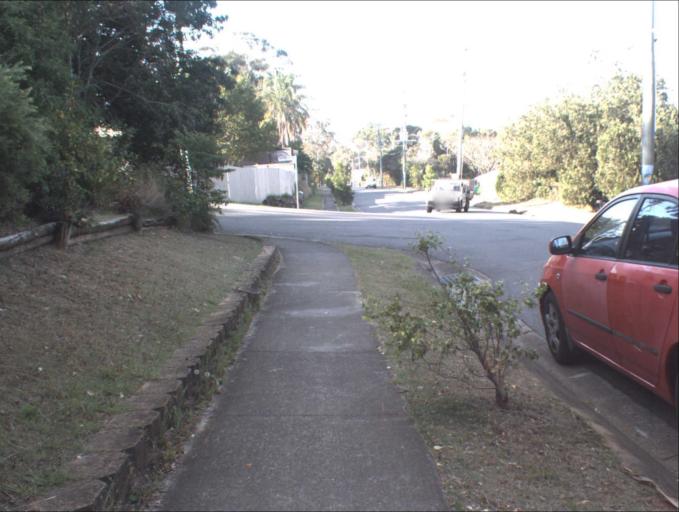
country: AU
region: Queensland
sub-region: Logan
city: Beenleigh
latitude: -27.6773
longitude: 153.2046
